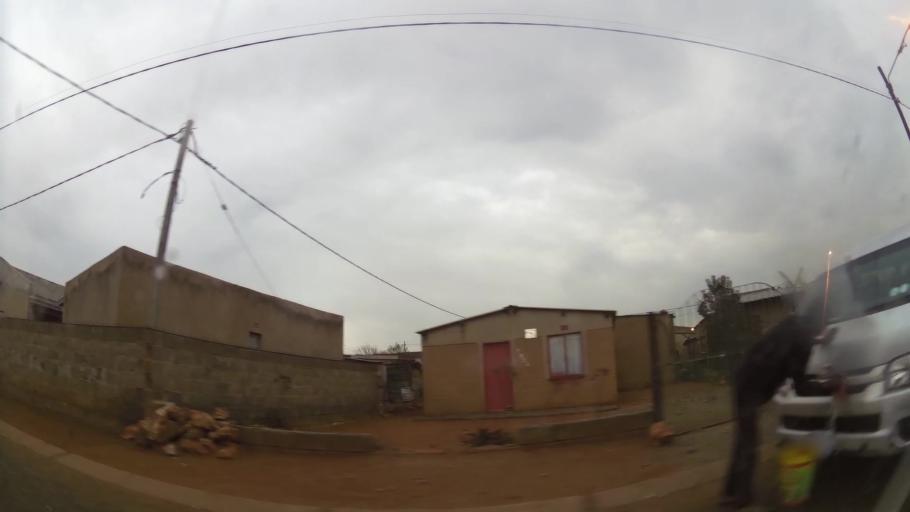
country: ZA
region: Gauteng
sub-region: Ekurhuleni Metropolitan Municipality
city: Germiston
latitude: -26.3812
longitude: 28.1790
